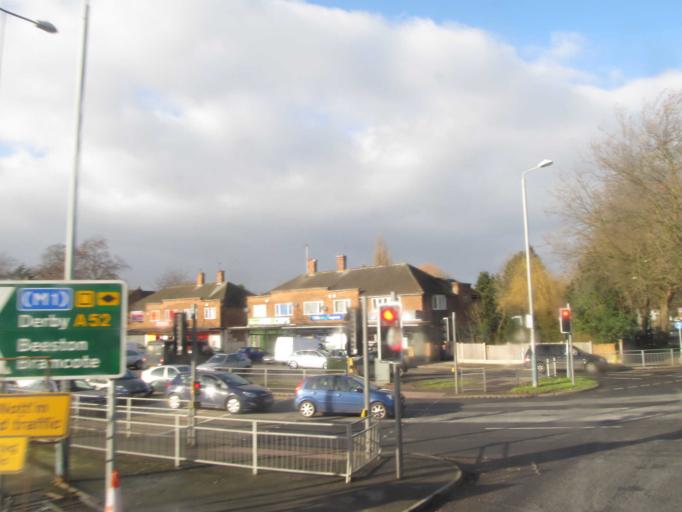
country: GB
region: England
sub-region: Nottinghamshire
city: Kimberley
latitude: 52.9389
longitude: -1.2165
